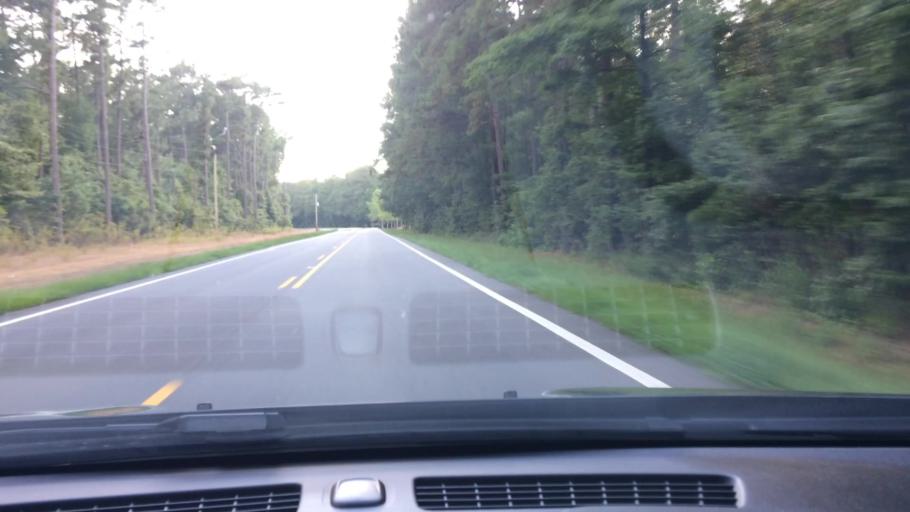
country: US
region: North Carolina
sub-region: Craven County
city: Vanceboro
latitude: 35.4285
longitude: -77.2073
